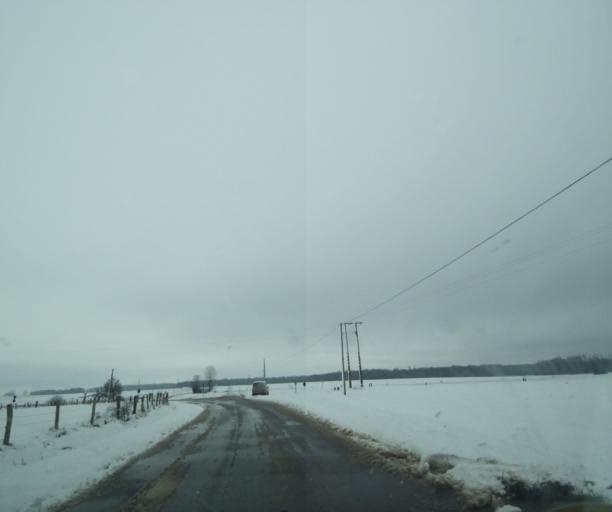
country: FR
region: Champagne-Ardenne
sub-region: Departement de la Haute-Marne
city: Montier-en-Der
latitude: 48.5119
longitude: 4.7755
